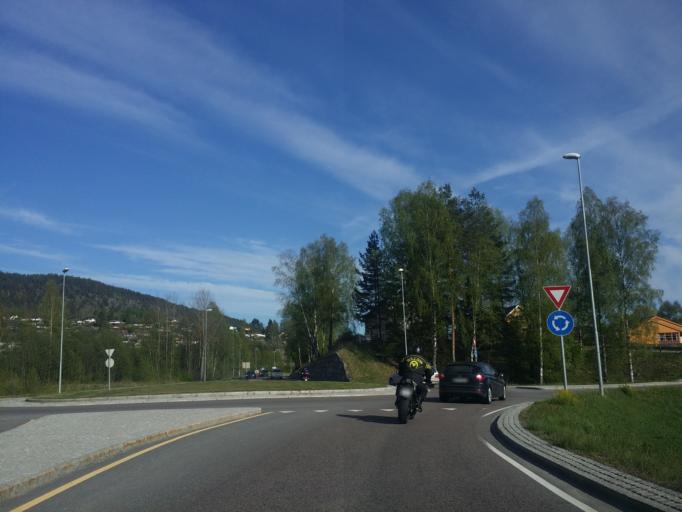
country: NO
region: Telemark
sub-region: Notodden
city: Notodden
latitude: 59.5764
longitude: 9.1896
